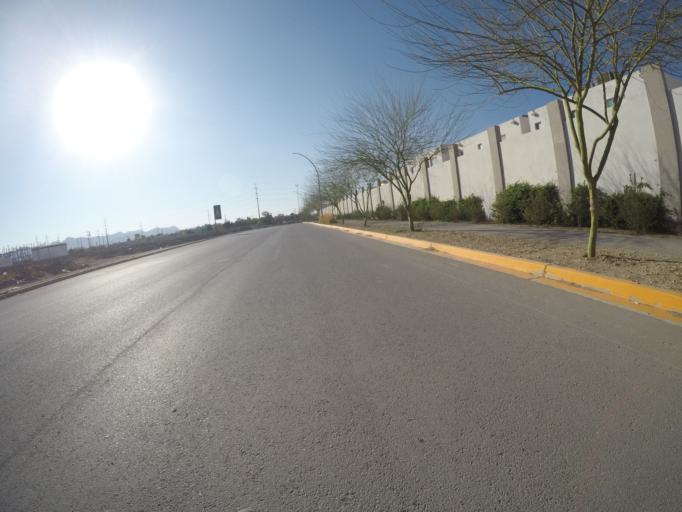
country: US
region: Texas
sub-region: El Paso County
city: Socorro
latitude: 31.7013
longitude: -106.3900
